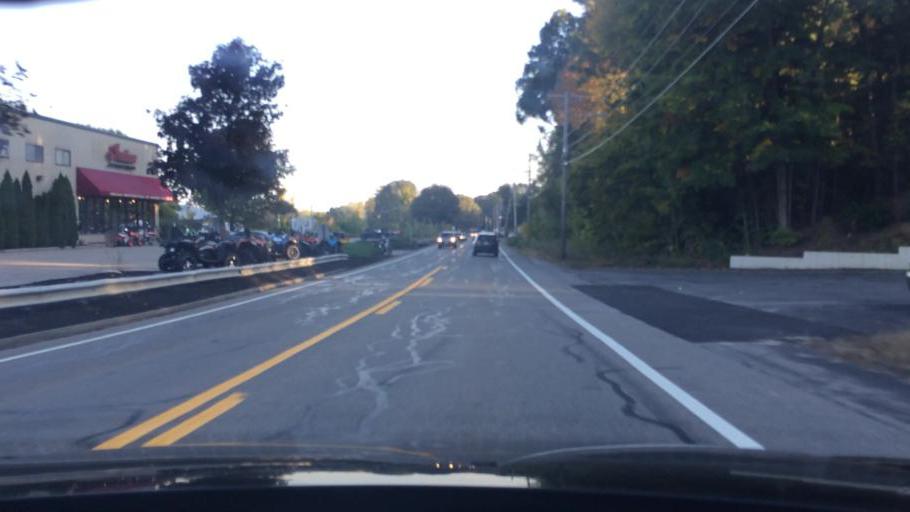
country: US
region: Massachusetts
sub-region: Middlesex County
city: Tyngsboro
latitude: 42.6548
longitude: -71.4019
